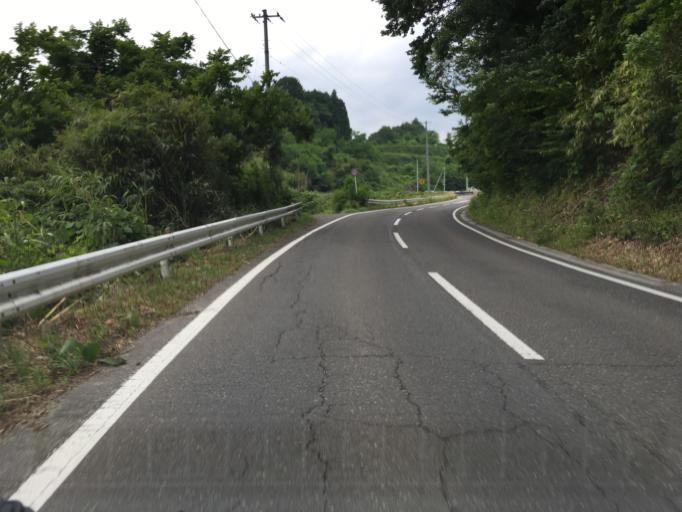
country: JP
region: Fukushima
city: Nihommatsu
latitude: 37.6293
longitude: 140.5398
